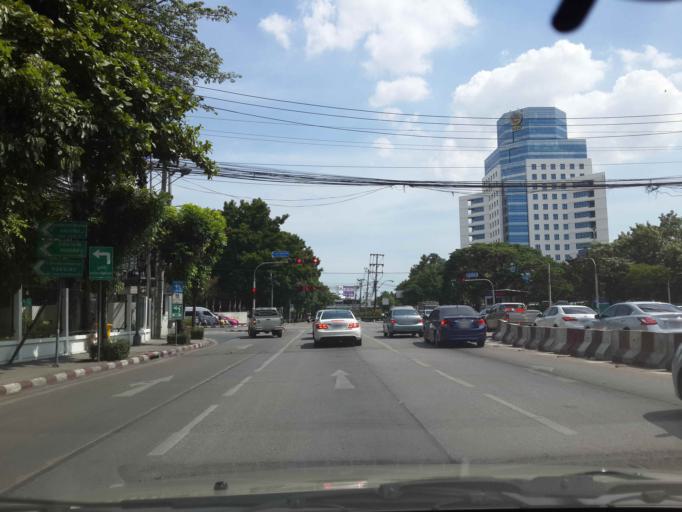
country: TH
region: Bangkok
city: Khlong Toei
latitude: 13.7152
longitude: 100.5656
